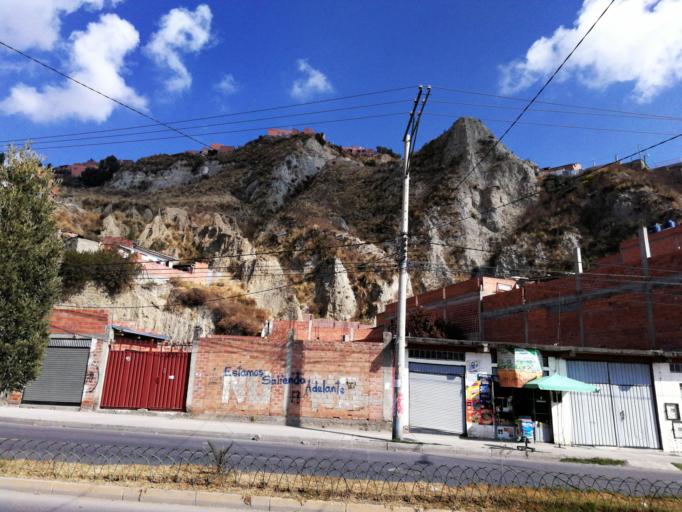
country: BO
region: La Paz
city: La Paz
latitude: -16.5288
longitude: -68.1376
